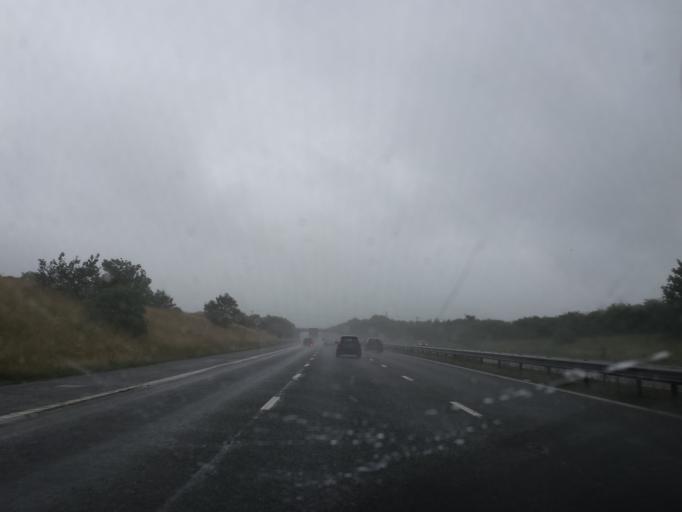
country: GB
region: England
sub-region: Leicestershire
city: Markfield
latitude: 52.6683
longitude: -1.2771
